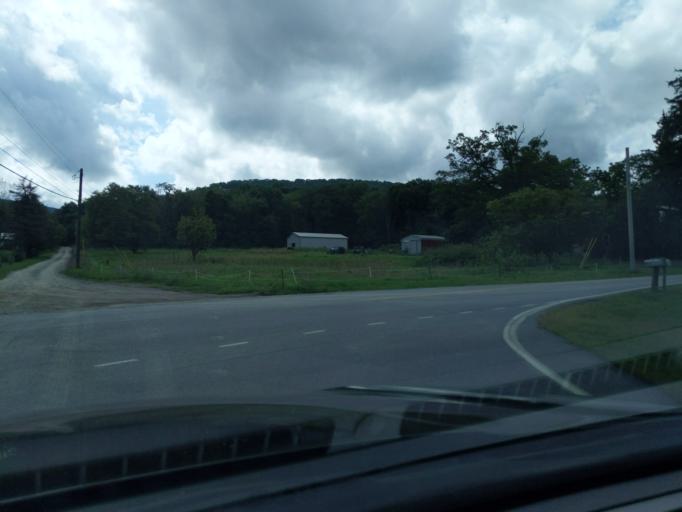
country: US
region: Pennsylvania
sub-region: Blair County
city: Hollidaysburg
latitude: 40.3931
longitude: -78.3989
